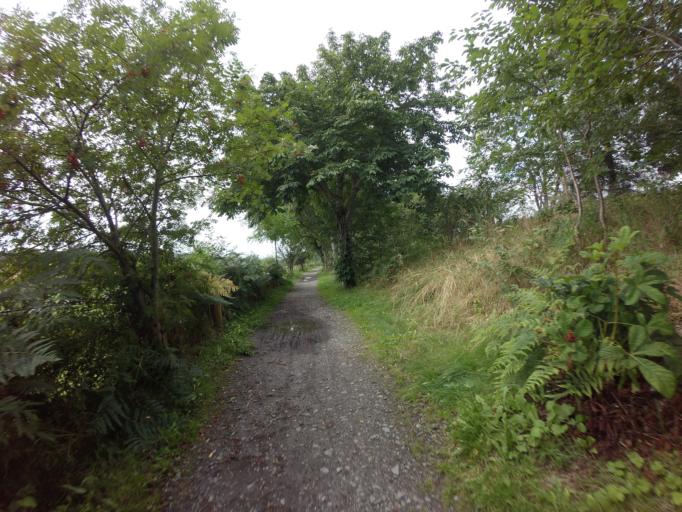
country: GB
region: Scotland
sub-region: Aberdeenshire
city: Banchory
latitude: 57.0554
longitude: -2.4375
